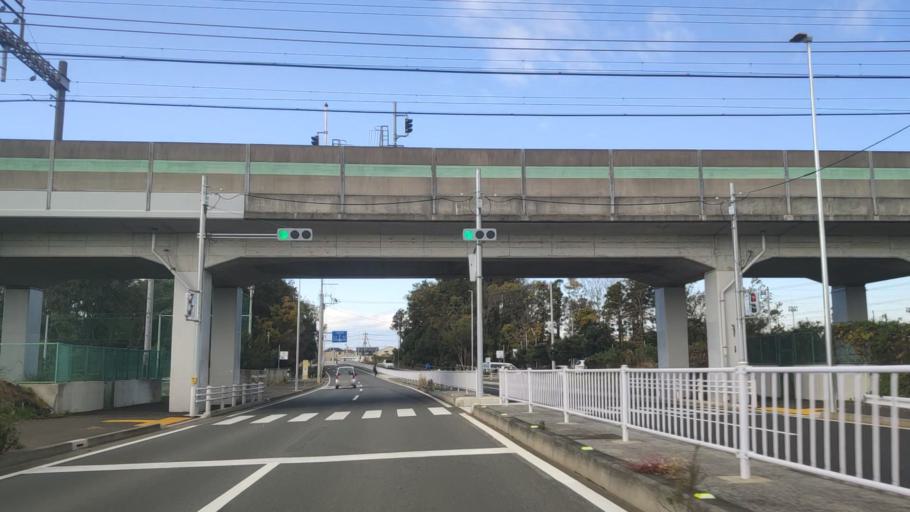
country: JP
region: Kanagawa
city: Minami-rinkan
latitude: 35.4264
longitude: 139.4876
